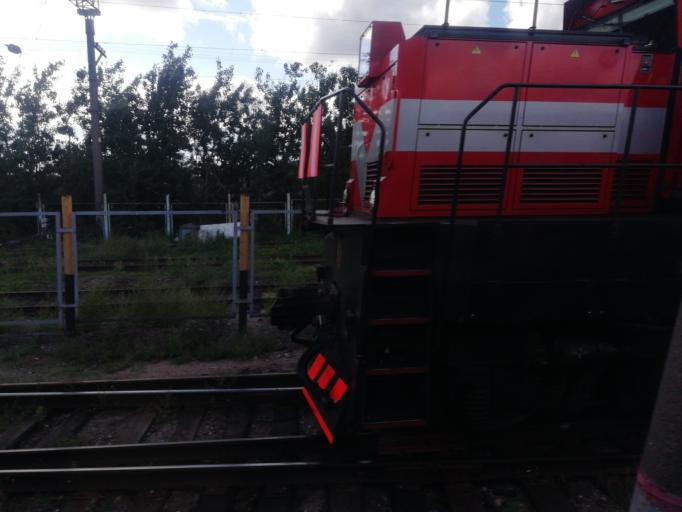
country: RU
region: Kaliningrad
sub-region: Gorod Kaliningrad
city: Kaliningrad
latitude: 54.6892
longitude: 20.4794
